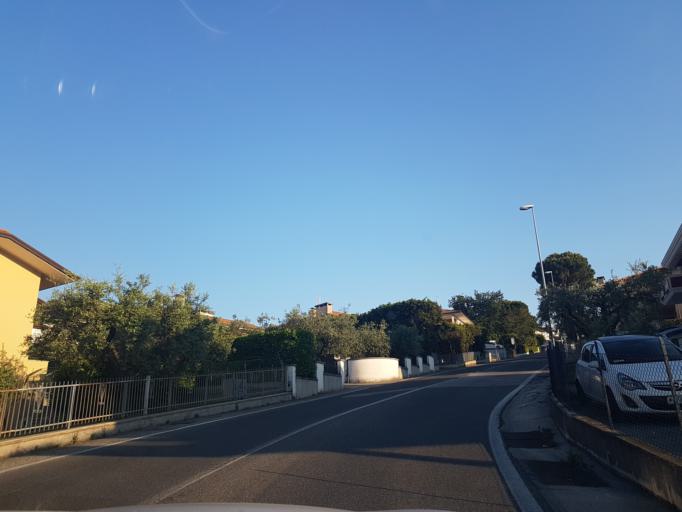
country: SM
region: Domagnano
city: Domagnano
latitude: 43.9596
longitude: 12.4689
